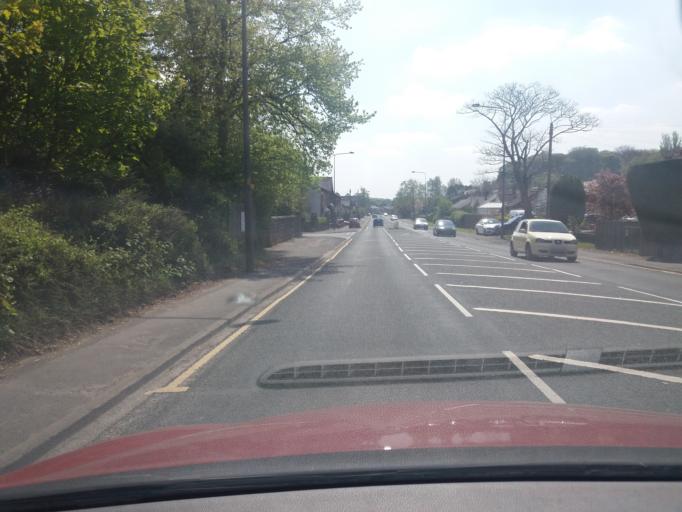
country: GB
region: England
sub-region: Lancashire
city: Clayton-le-Woods
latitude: 53.6979
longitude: -2.6390
